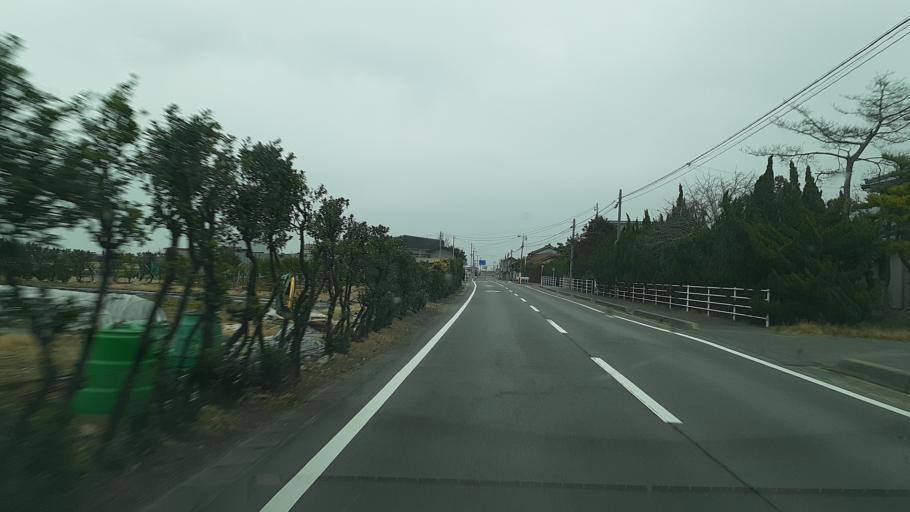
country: JP
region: Niigata
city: Kameda-honcho
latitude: 37.8606
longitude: 139.0616
